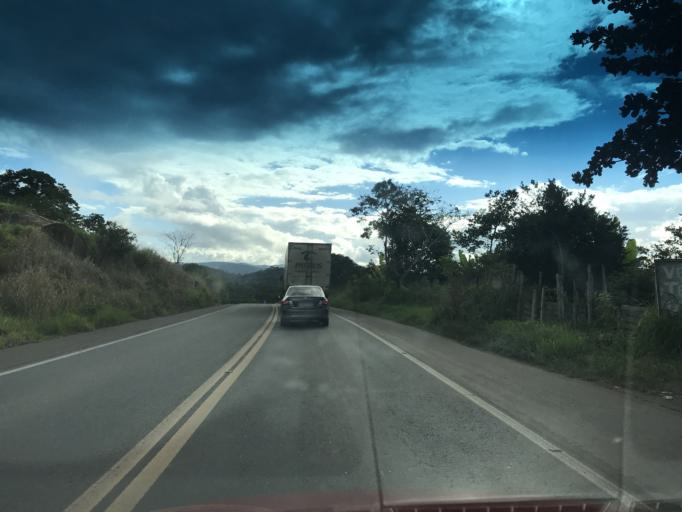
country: BR
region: Bahia
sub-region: Ibirapitanga
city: Ibirapitanga
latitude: -14.1504
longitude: -39.3343
